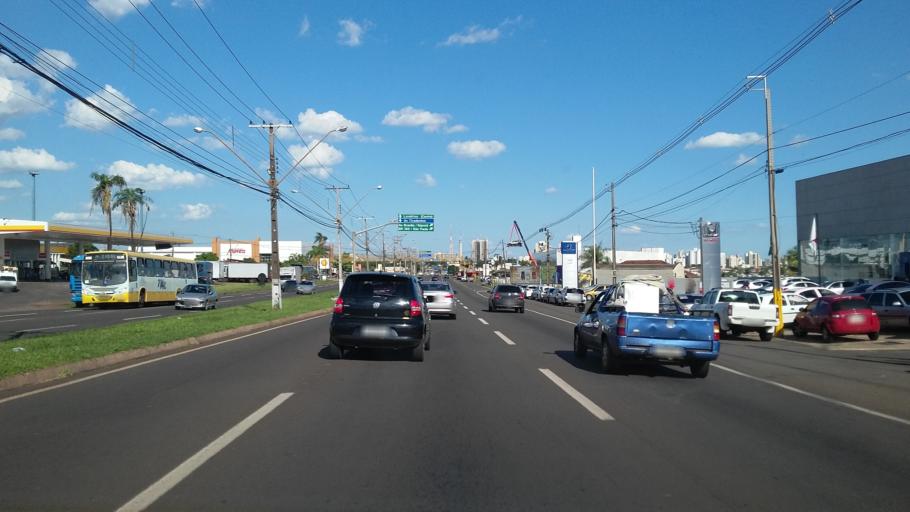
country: BR
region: Parana
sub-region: Londrina
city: Londrina
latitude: -23.2975
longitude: -51.2005
